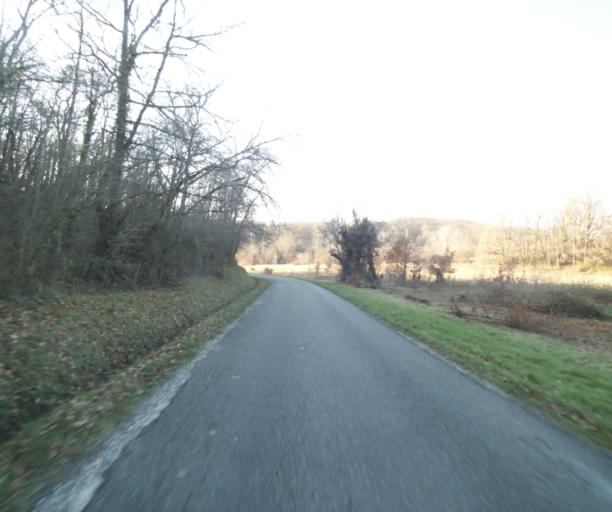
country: FR
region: Midi-Pyrenees
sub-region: Departement du Tarn-et-Garonne
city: Moissac
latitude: 44.1294
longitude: 1.1346
